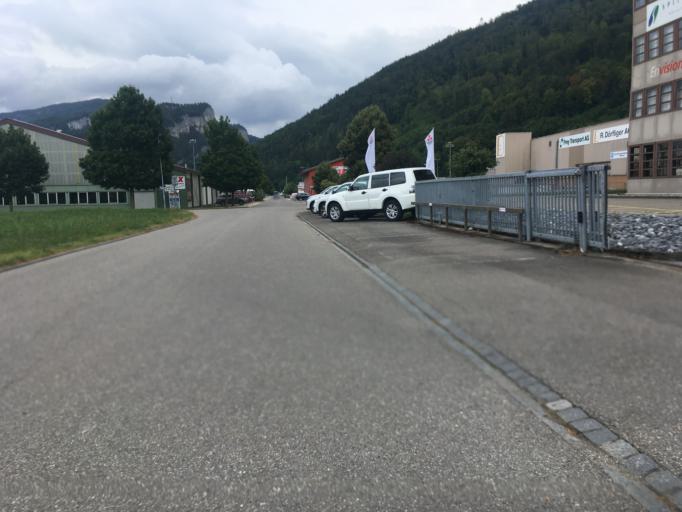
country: CH
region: Solothurn
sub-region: Bezirk Thal
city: Balsthal
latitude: 47.3083
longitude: 7.6771
